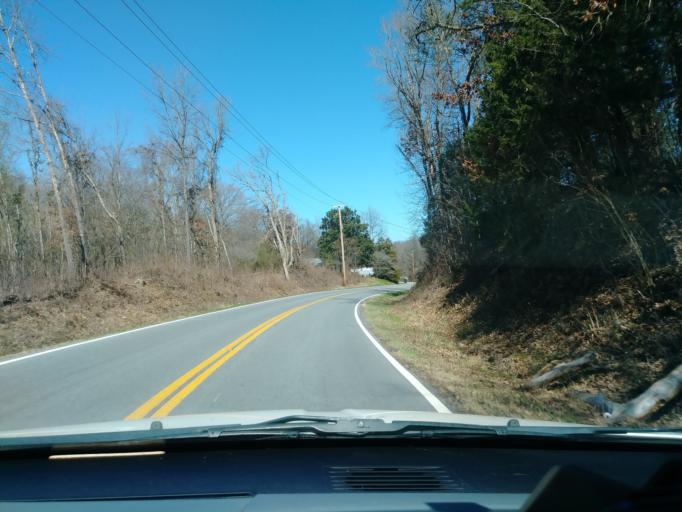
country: US
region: Tennessee
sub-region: Cocke County
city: Newport
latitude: 35.9787
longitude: -83.0608
